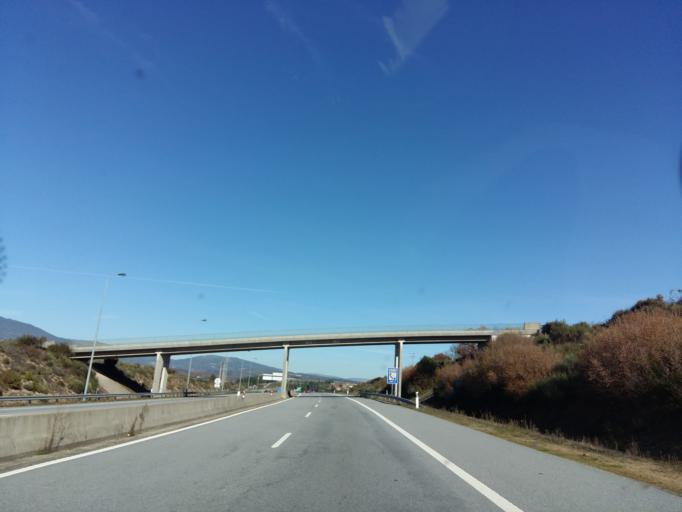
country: PT
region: Castelo Branco
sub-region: Covilha
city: Covilha
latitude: 40.2311
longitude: -7.4860
